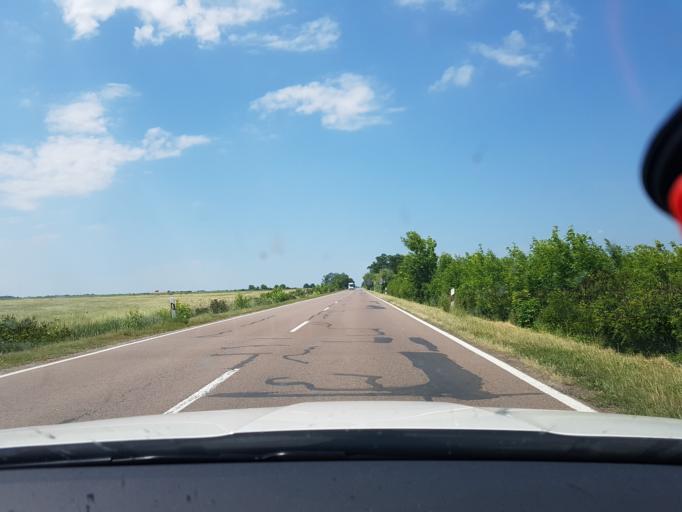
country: HU
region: Hajdu-Bihar
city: Hortobagy
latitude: 47.5867
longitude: 21.1077
